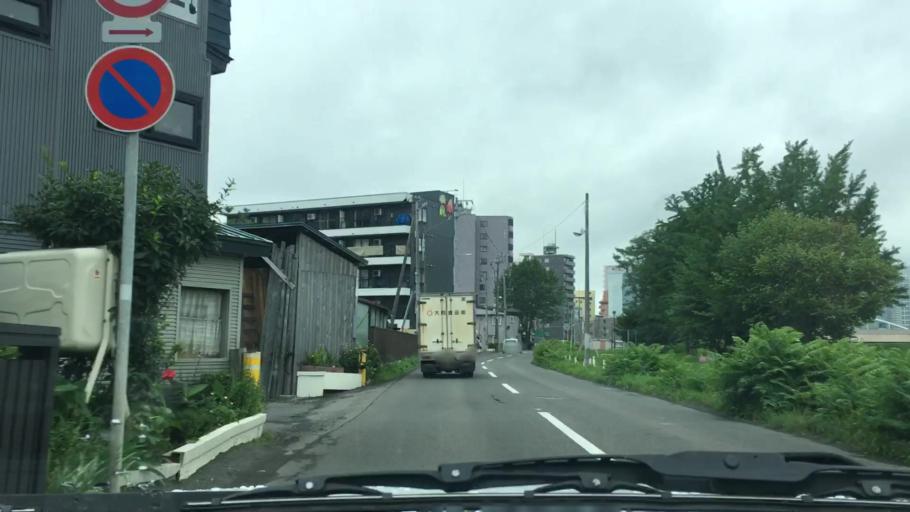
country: JP
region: Hokkaido
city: Sapporo
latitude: 43.0596
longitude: 141.3692
